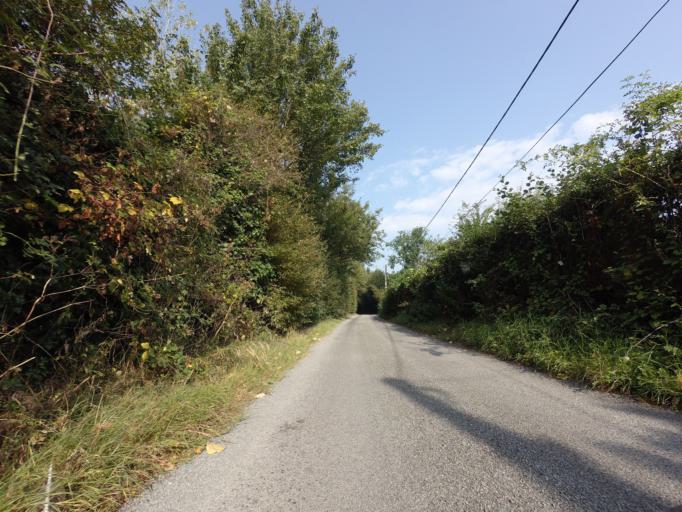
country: GB
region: England
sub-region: Kent
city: Headcorn
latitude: 51.1291
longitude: 0.6537
